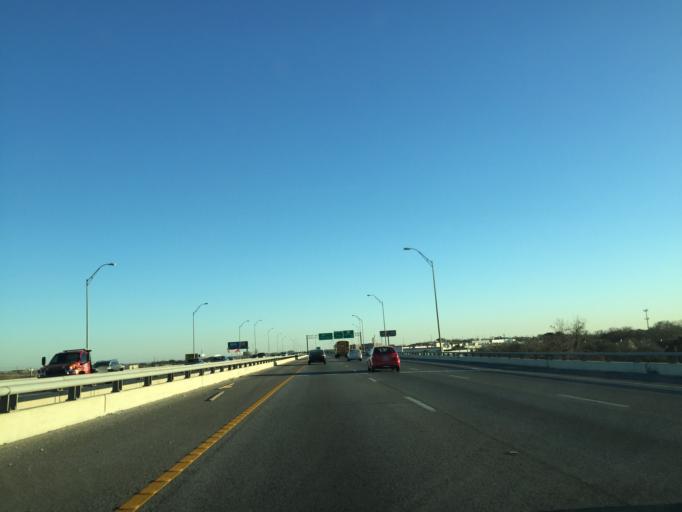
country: US
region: Texas
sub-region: Travis County
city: Austin
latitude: 30.3569
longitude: -97.7157
